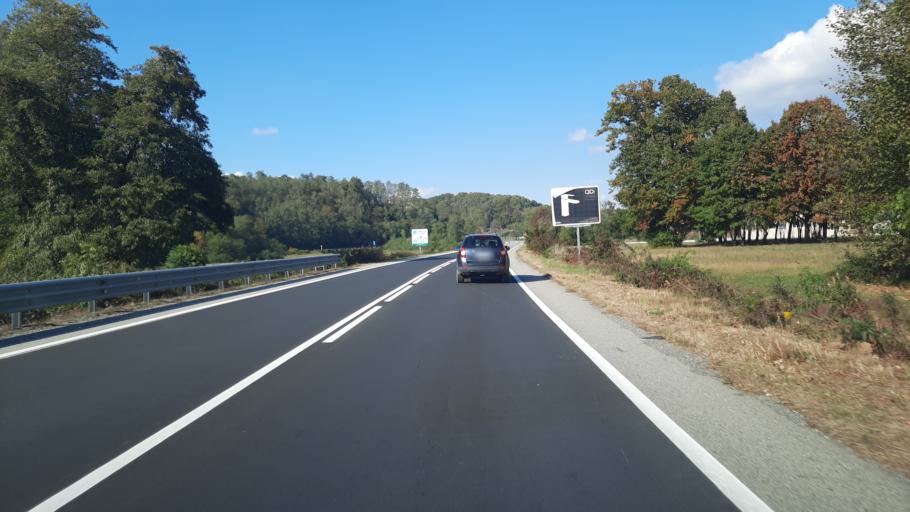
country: IT
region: Piedmont
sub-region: Provincia di Novara
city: Gargallo
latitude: 45.7340
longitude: 8.4329
